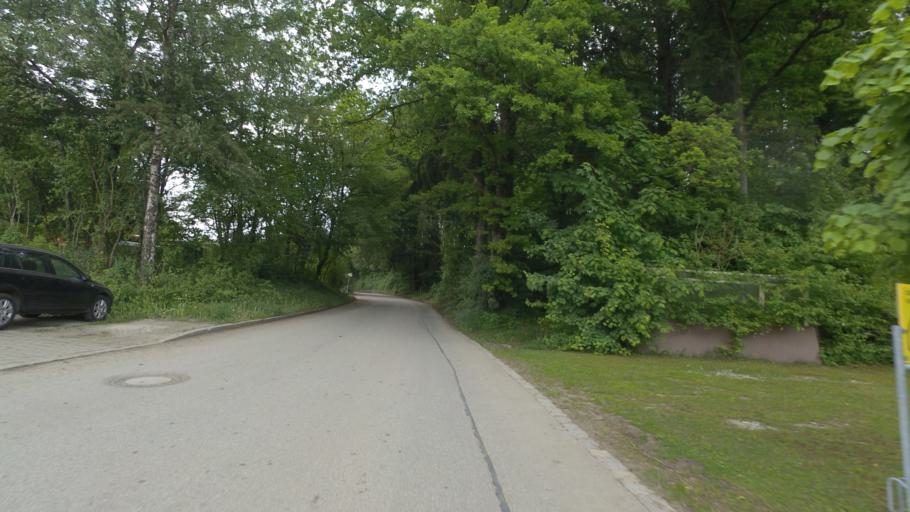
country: DE
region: Bavaria
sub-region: Upper Bavaria
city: Chieming
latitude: 47.9268
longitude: 12.5547
